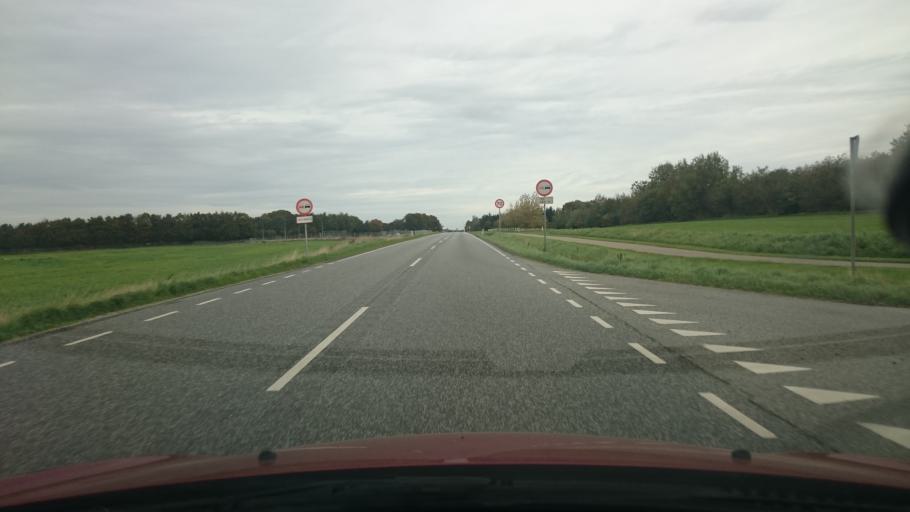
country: DK
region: Central Jutland
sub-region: Randers Kommune
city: Spentrup
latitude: 56.5926
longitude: 10.1319
